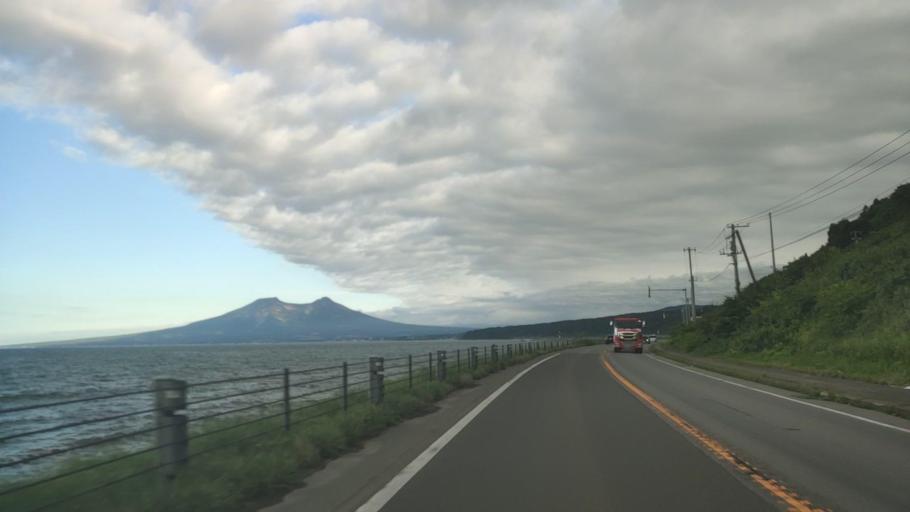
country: JP
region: Hokkaido
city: Nanae
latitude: 42.1468
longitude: 140.4988
